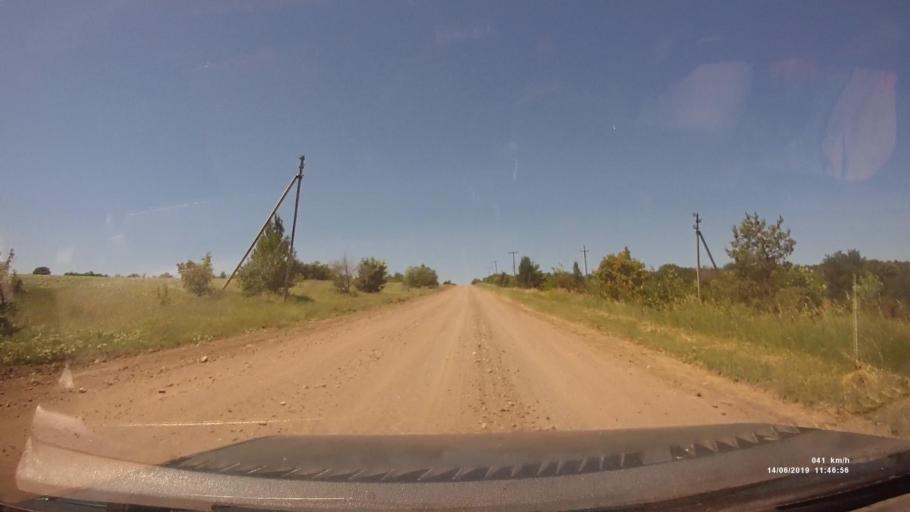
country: RU
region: Rostov
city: Kazanskaya
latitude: 49.8511
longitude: 41.3000
